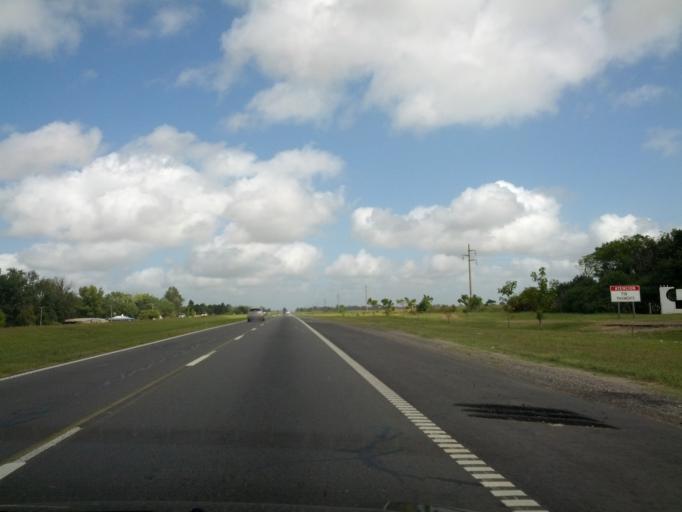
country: AR
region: Buenos Aires
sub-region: Partido de Lujan
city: Lujan
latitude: -34.6176
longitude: -59.2012
